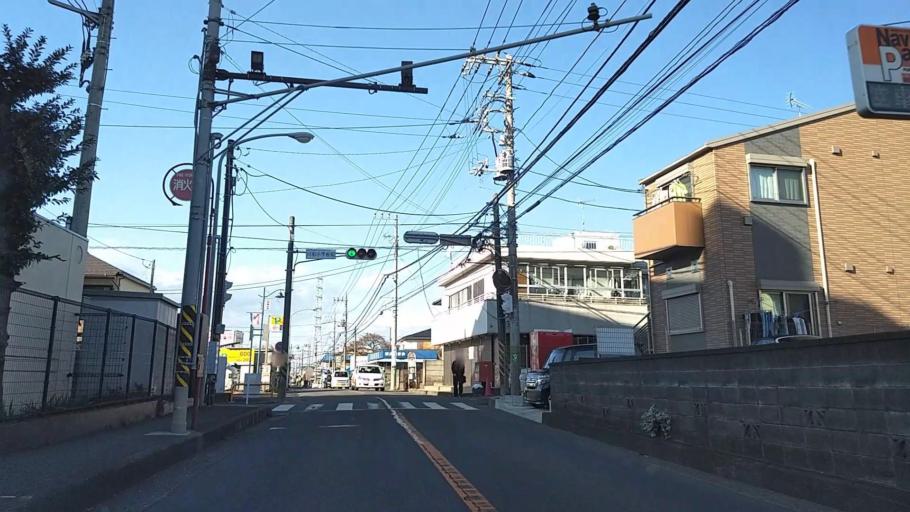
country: JP
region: Tokyo
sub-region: Machida-shi
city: Machida
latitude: 35.5300
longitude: 139.5480
